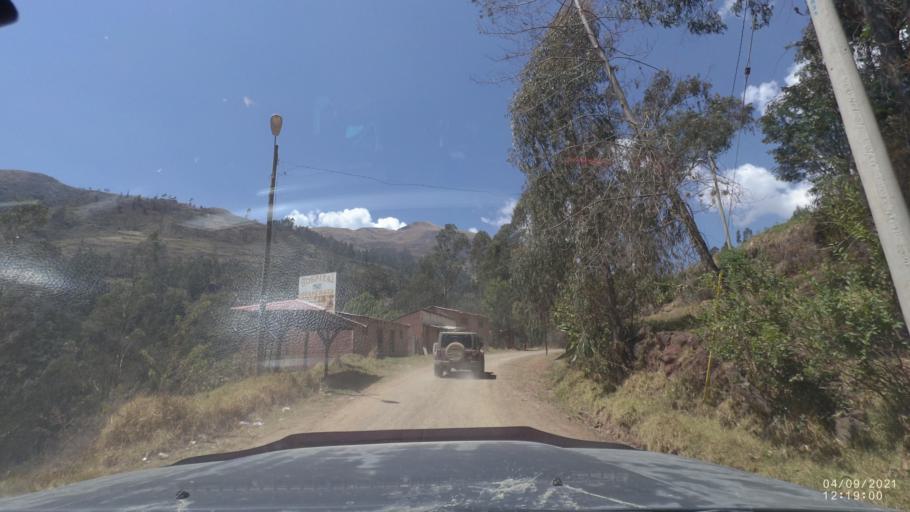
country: BO
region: Cochabamba
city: Colchani
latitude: -17.2362
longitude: -66.5311
